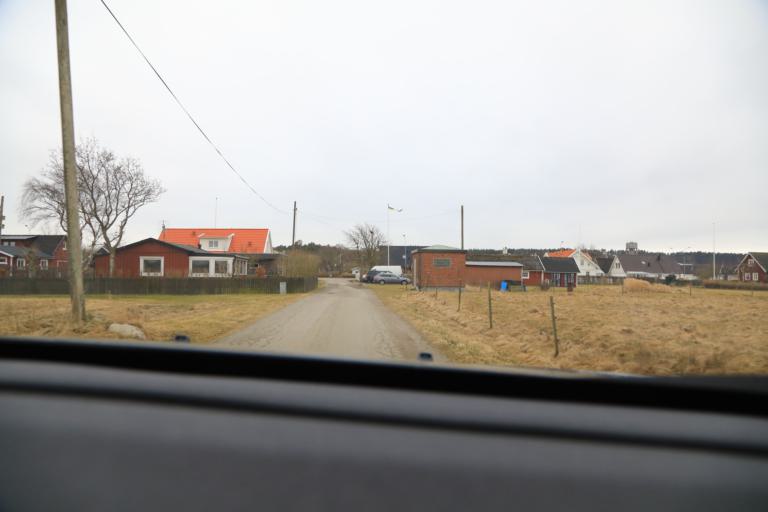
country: SE
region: Halland
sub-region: Kungsbacka Kommun
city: Frillesas
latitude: 57.2409
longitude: 12.1250
